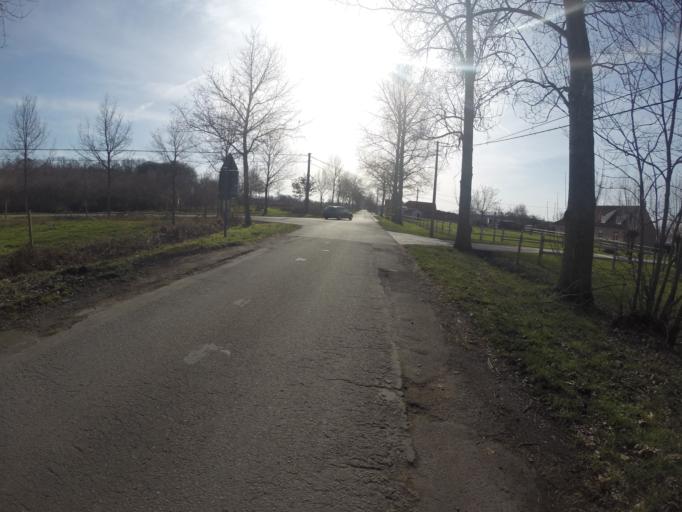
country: BE
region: Flanders
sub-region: Provincie West-Vlaanderen
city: Oostkamp
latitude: 51.1162
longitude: 3.2398
